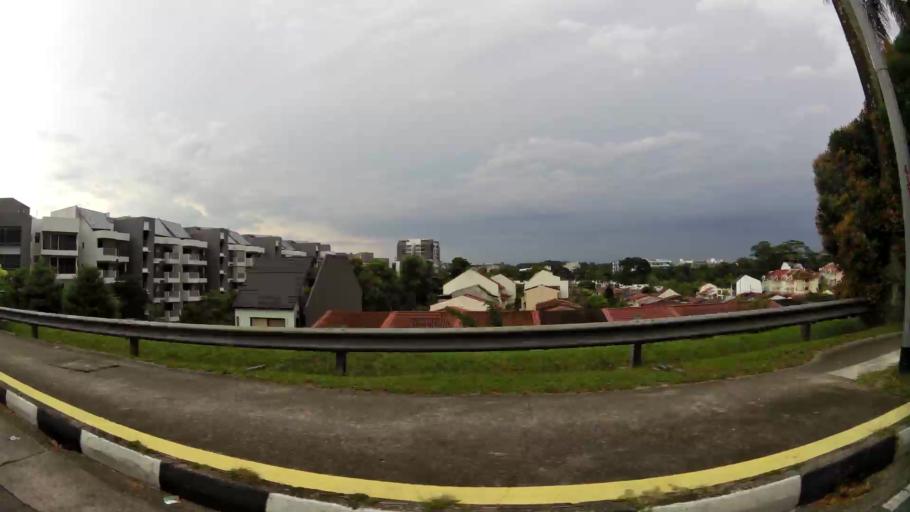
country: SG
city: Singapore
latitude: 1.3790
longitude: 103.8296
